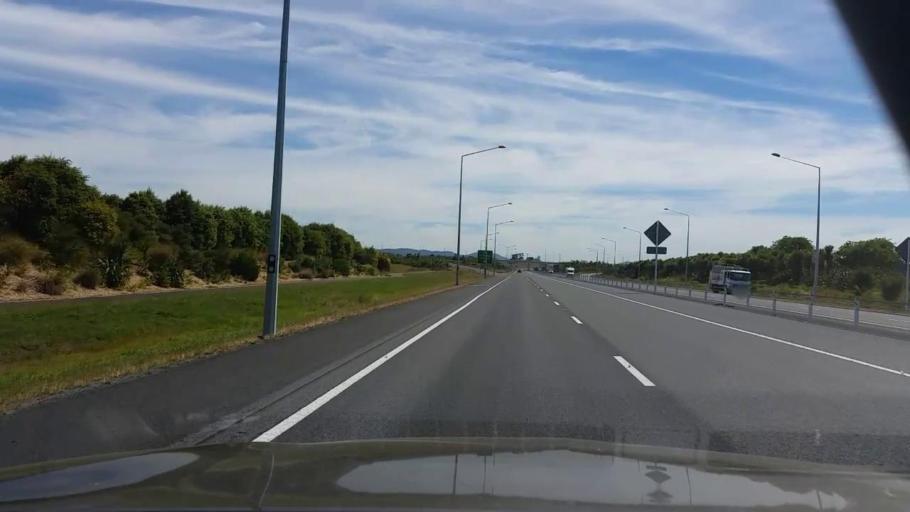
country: NZ
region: Waikato
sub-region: Hamilton City
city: Hamilton
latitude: -37.7384
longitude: 175.2119
